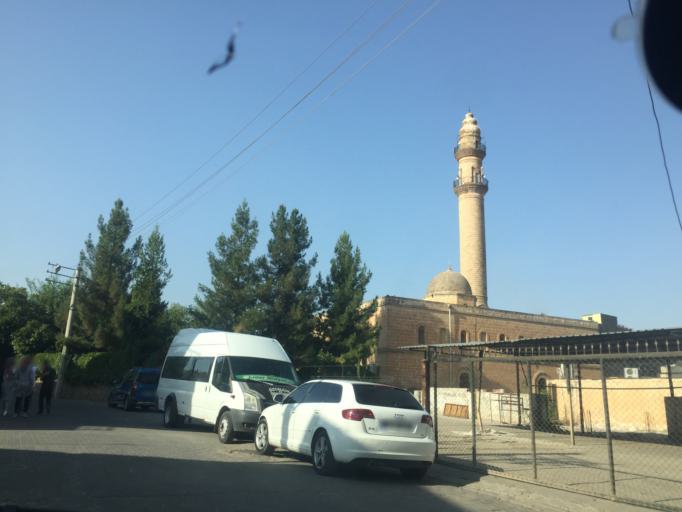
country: TR
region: Mardin
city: Midyat
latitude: 37.4139
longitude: 41.3728
